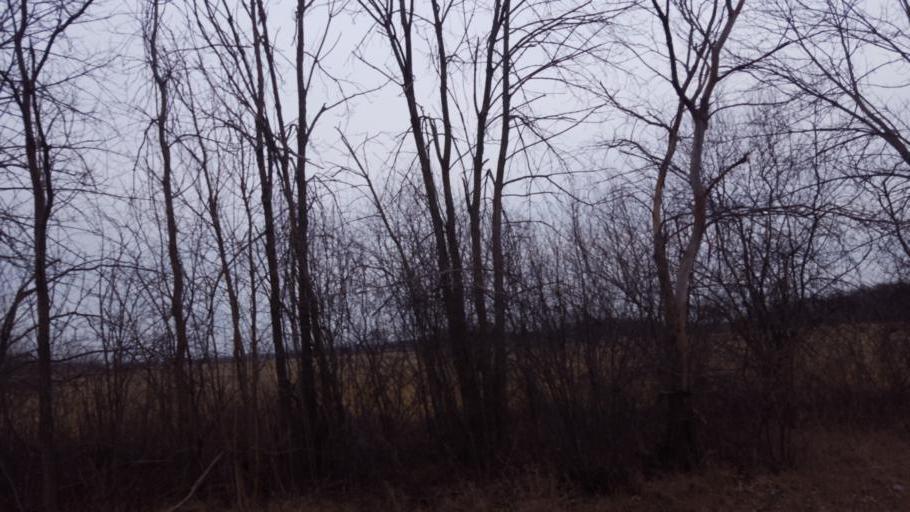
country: US
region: Ohio
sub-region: Crawford County
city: Crestline
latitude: 40.7803
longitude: -82.7263
